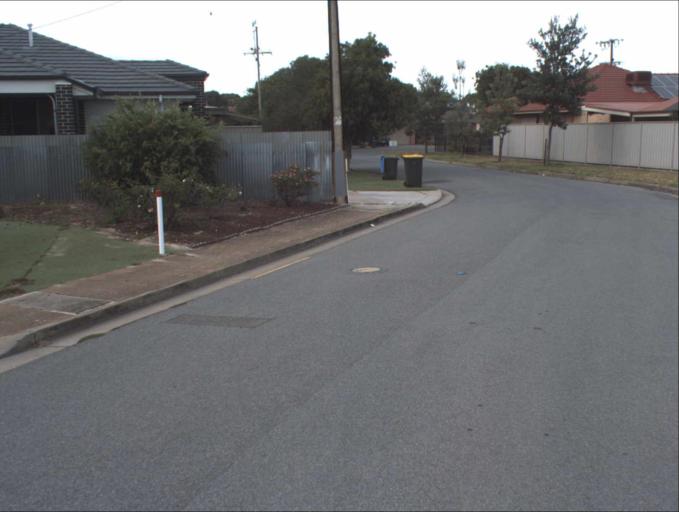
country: AU
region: South Australia
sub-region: Port Adelaide Enfield
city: Birkenhead
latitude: -34.8288
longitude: 138.4980
